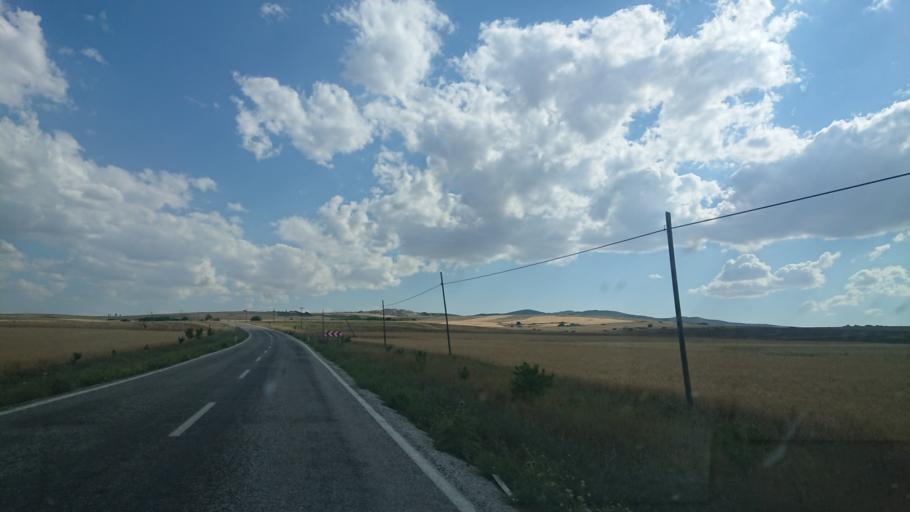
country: TR
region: Aksaray
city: Sariyahsi
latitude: 38.9393
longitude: 33.8337
